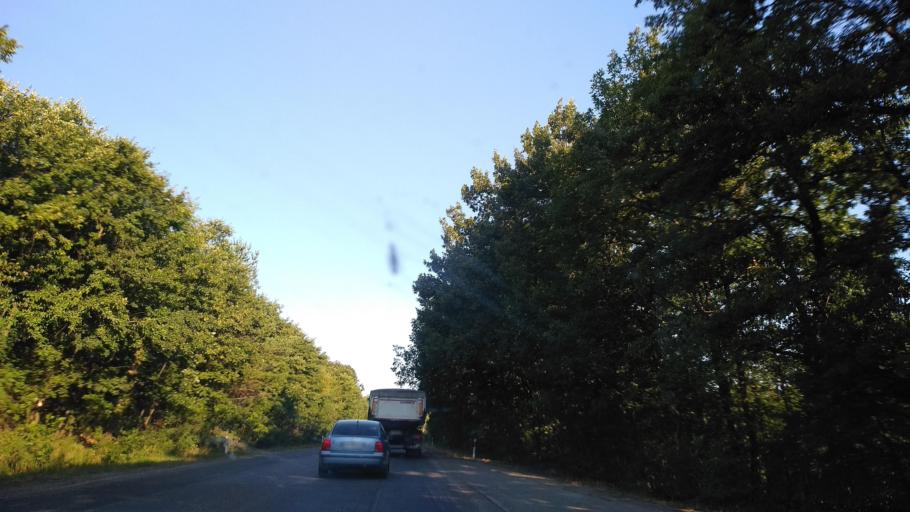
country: BG
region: Gabrovo
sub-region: Obshtina Dryanovo
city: Dryanovo
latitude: 43.0885
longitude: 25.5037
